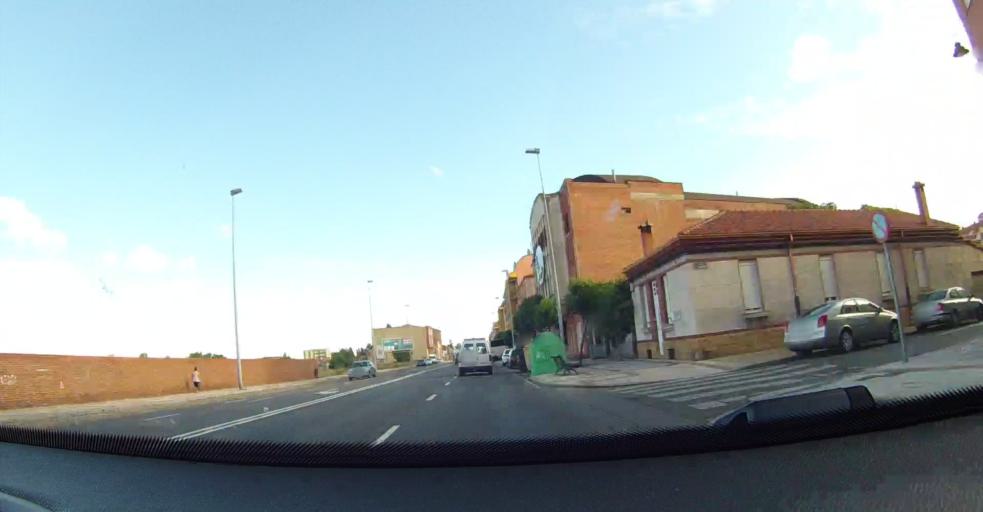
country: ES
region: Castille and Leon
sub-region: Provincia de Leon
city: Leon
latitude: 42.5891
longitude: -5.5846
